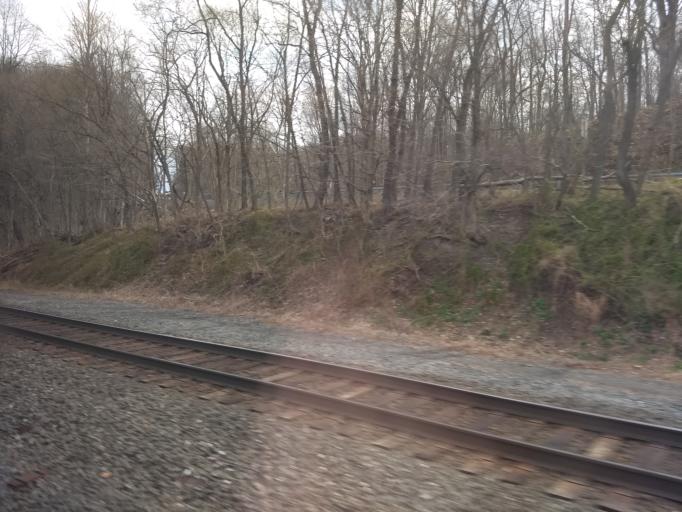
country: US
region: Pennsylvania
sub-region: Mifflin County
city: Lewistown
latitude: 40.5266
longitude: -77.6472
